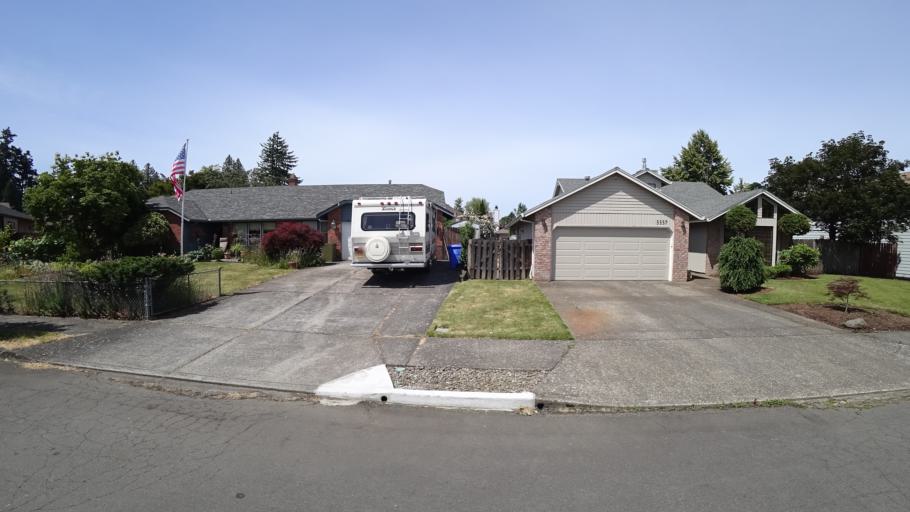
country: US
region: Oregon
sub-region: Multnomah County
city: Fairview
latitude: 45.5474
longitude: -122.5012
